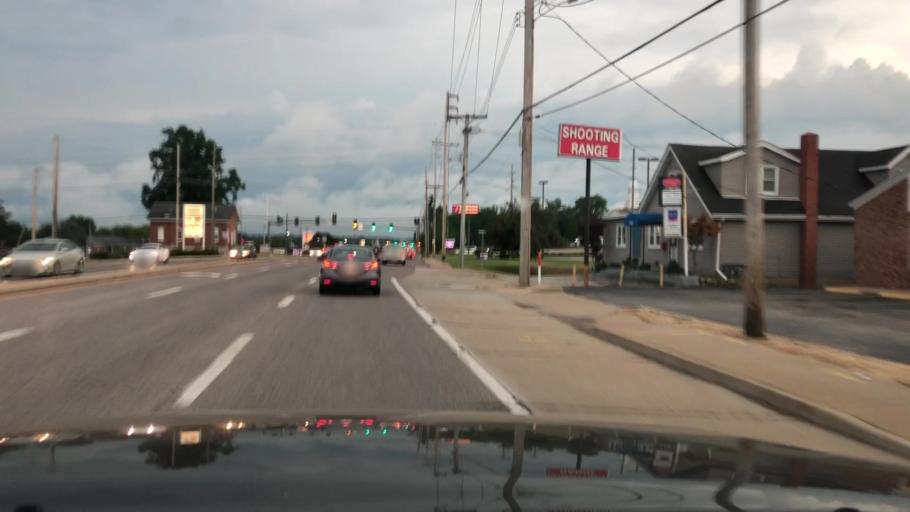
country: US
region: Missouri
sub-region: Saint Louis County
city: Saint Ann
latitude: 38.7411
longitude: -90.4052
